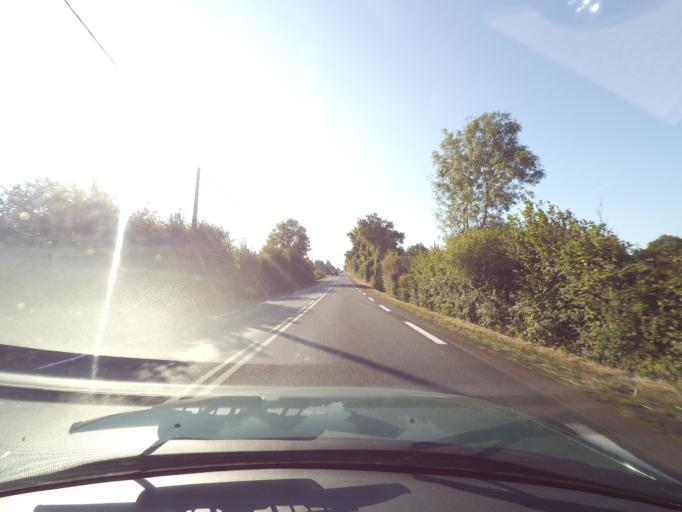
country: FR
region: Poitou-Charentes
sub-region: Departement des Deux-Sevres
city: Chiche
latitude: 46.8081
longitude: -0.3831
